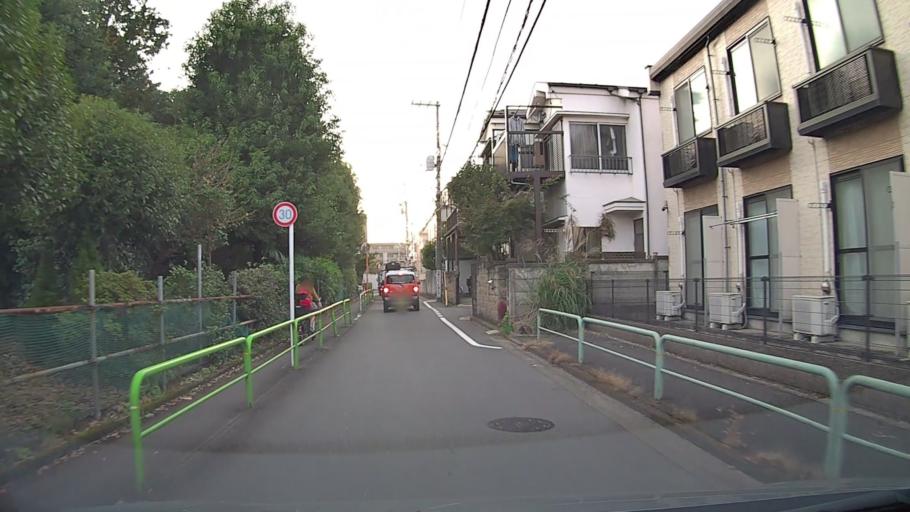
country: JP
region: Saitama
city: Wako
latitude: 35.7508
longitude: 139.6211
